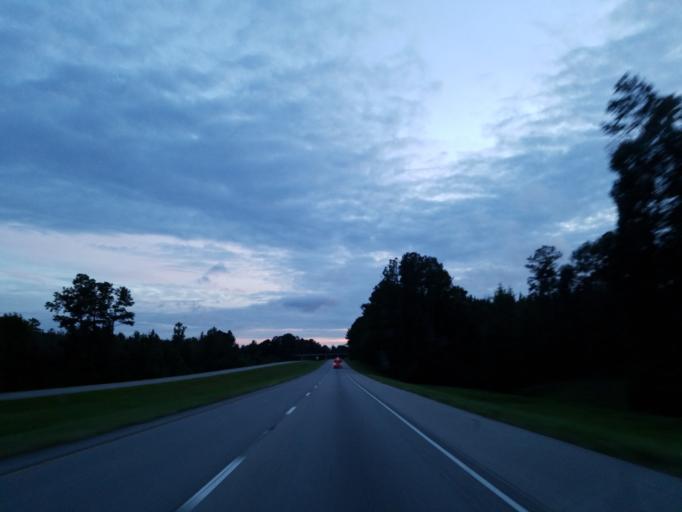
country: US
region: Mississippi
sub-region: Clarke County
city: Stonewall
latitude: 32.1938
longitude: -88.8515
